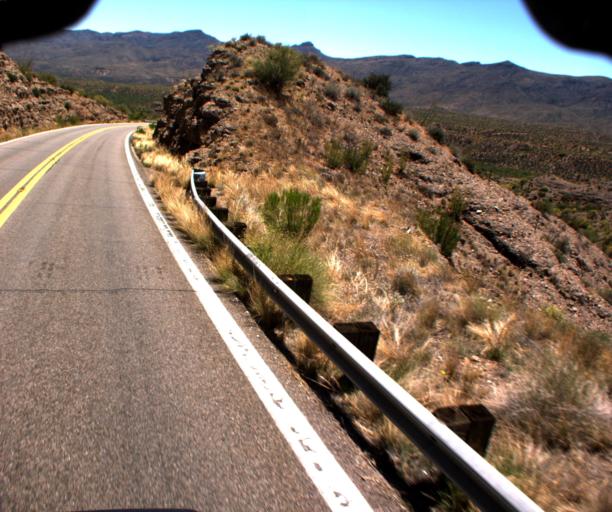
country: US
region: Arizona
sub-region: Pinal County
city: Kearny
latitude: 33.1607
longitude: -110.8045
